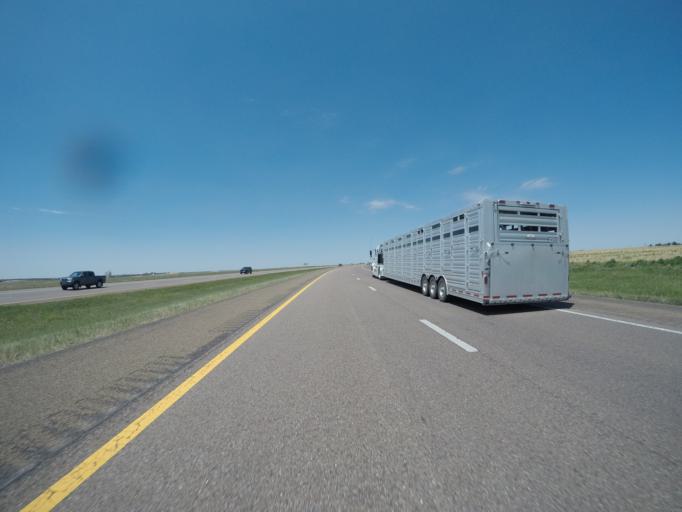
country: US
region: Kansas
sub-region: Logan County
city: Oakley
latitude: 39.1124
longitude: -100.7954
